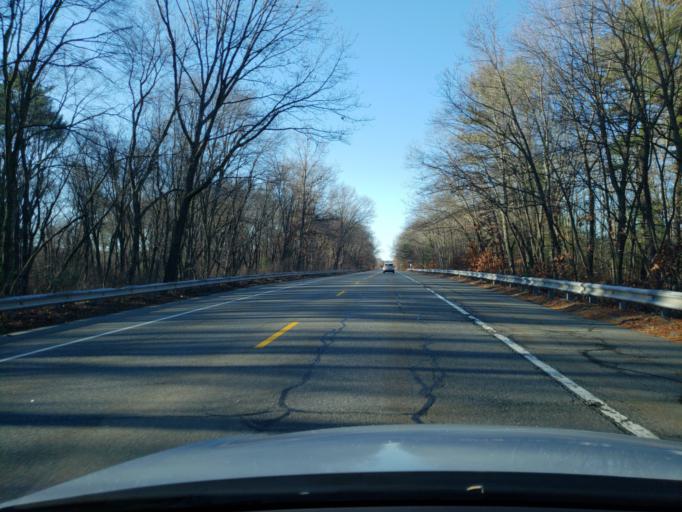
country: US
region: Massachusetts
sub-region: Middlesex County
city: Wilmington
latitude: 42.5954
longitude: -71.1407
